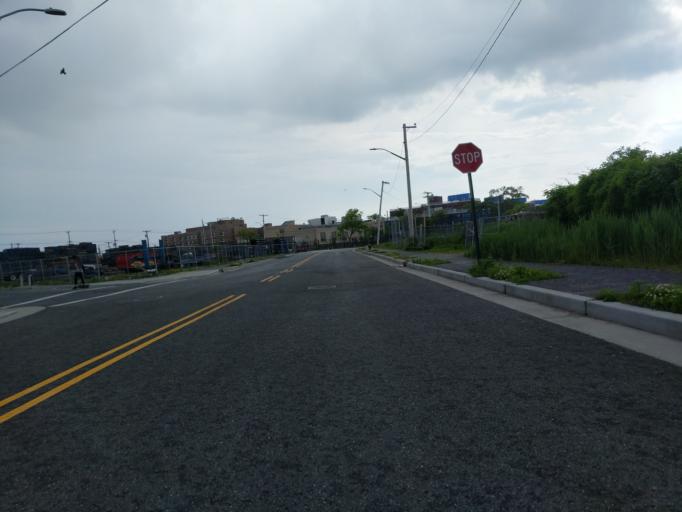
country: US
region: New York
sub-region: Nassau County
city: Inwood
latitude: 40.5972
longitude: -73.7791
